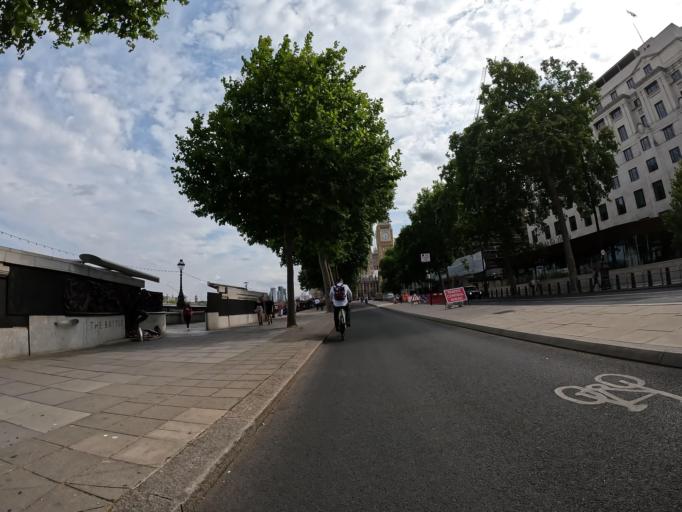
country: GB
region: England
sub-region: Greater London
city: Bromley
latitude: 51.3988
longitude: 0.0323
